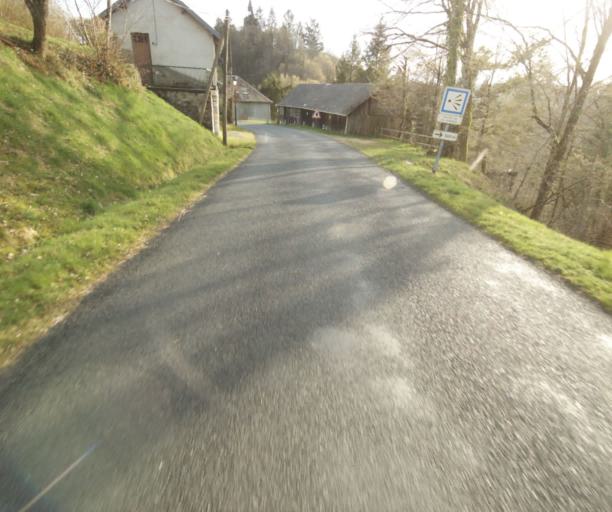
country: FR
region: Limousin
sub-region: Departement de la Correze
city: Naves
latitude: 45.3477
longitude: 1.8177
